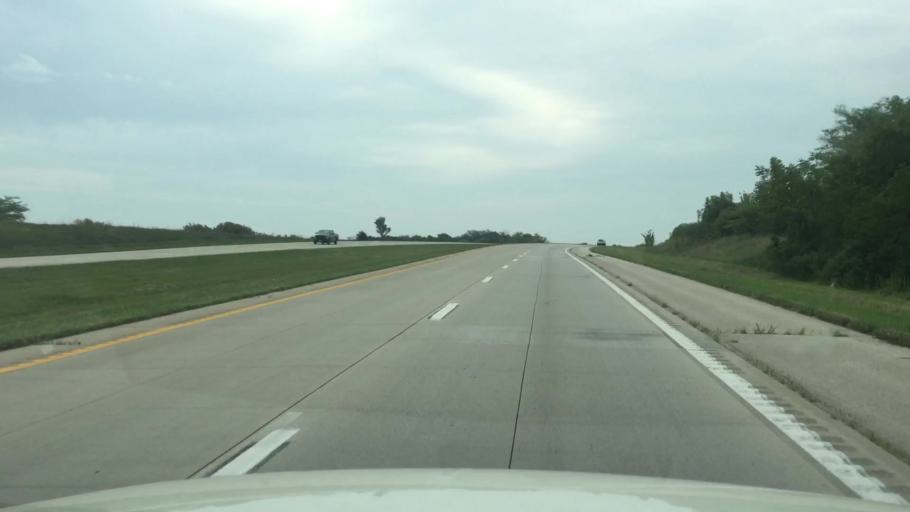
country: US
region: Missouri
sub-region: Daviess County
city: Gallatin
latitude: 39.9771
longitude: -94.0944
